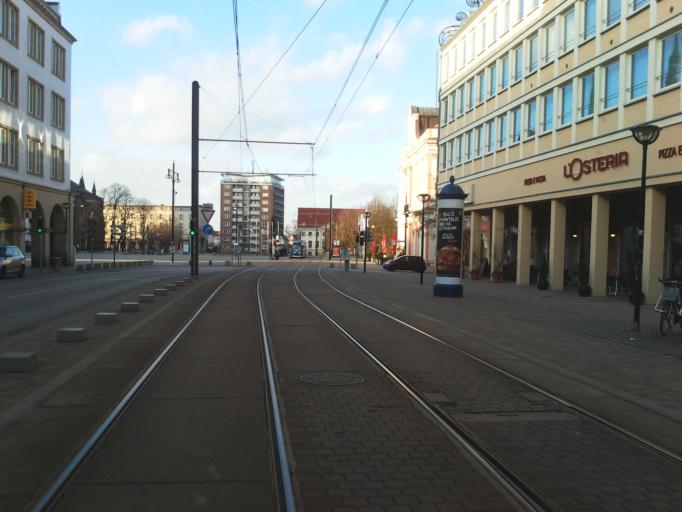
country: DE
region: Mecklenburg-Vorpommern
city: Rostock
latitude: 54.0878
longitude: 12.1408
